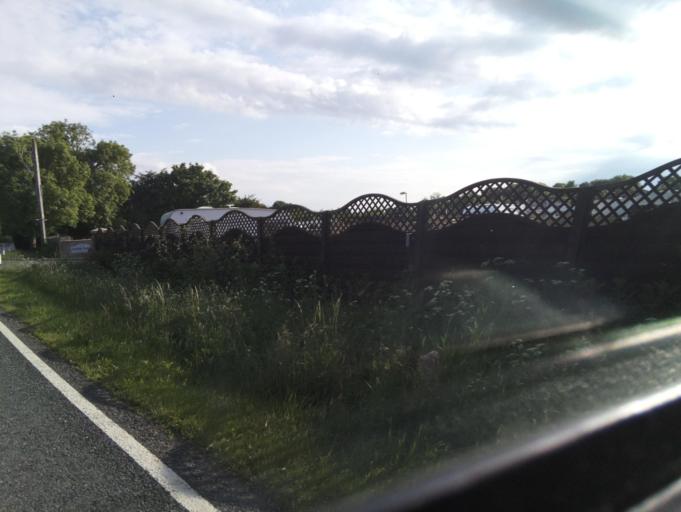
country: GB
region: England
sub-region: Lincolnshire
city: Great Gonerby
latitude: 53.0506
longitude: -0.6449
